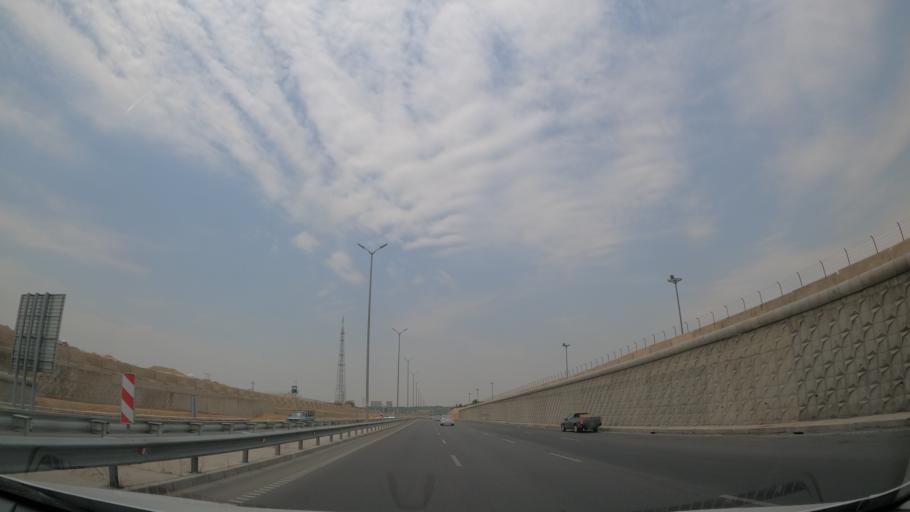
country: IR
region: Tehran
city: Shahr-e Qods
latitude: 35.7412
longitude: 51.2403
